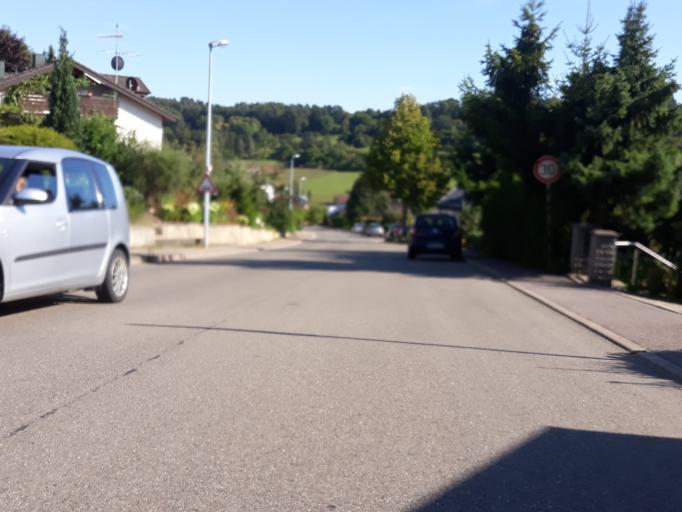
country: DE
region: Baden-Wuerttemberg
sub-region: Karlsruhe Region
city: Gechingen
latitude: 48.6810
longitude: 8.8547
